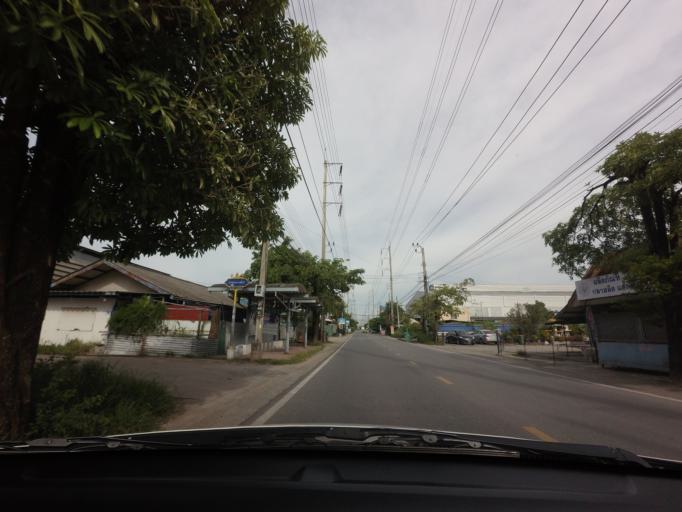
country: TH
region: Bangkok
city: Bang Na
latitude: 13.6197
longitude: 100.6562
